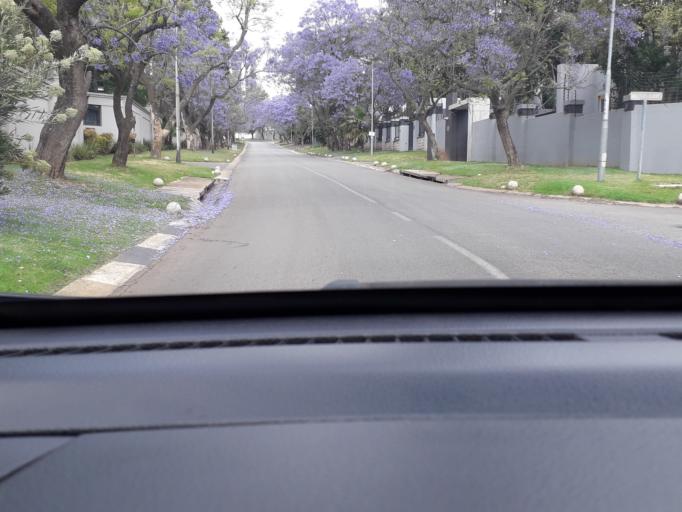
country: ZA
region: Gauteng
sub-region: City of Johannesburg Metropolitan Municipality
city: Modderfontein
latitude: -26.0934
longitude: 28.0598
